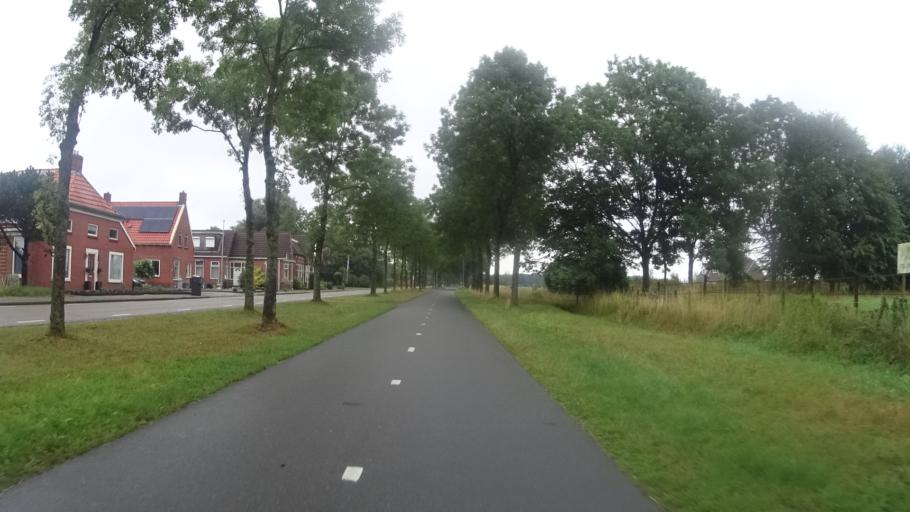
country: NL
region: Groningen
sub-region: Gemeente  Oldambt
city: Winschoten
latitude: 53.1637
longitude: 7.0844
